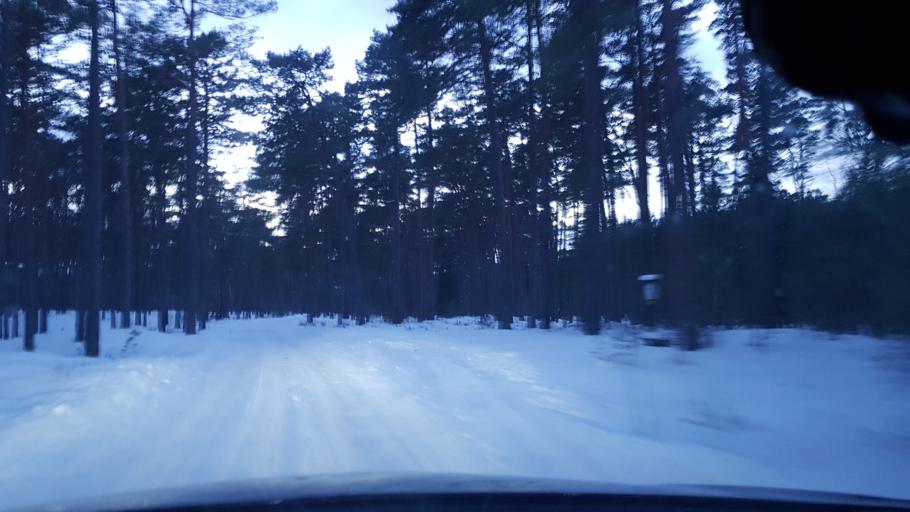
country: EE
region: Laeaene
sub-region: Ridala Parish
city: Uuemoisa
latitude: 59.2169
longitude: 23.6010
